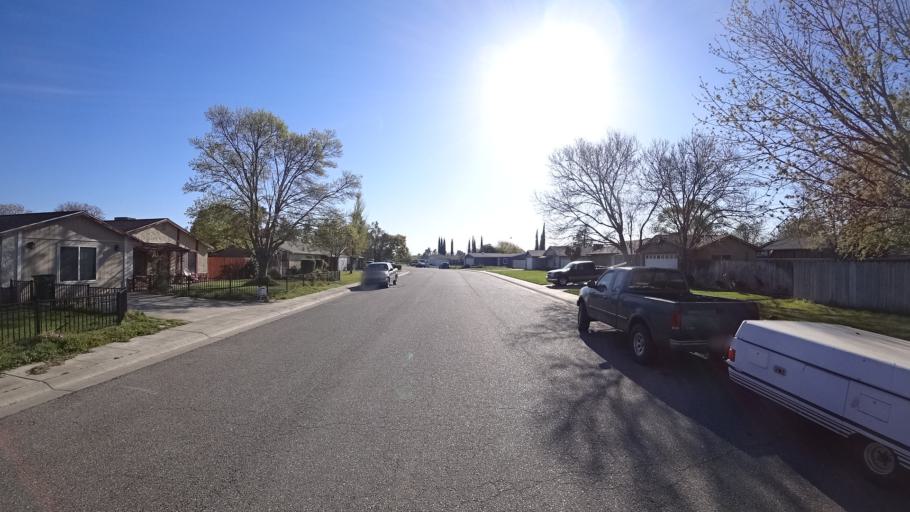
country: US
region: California
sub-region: Glenn County
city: Orland
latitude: 39.7605
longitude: -122.2226
